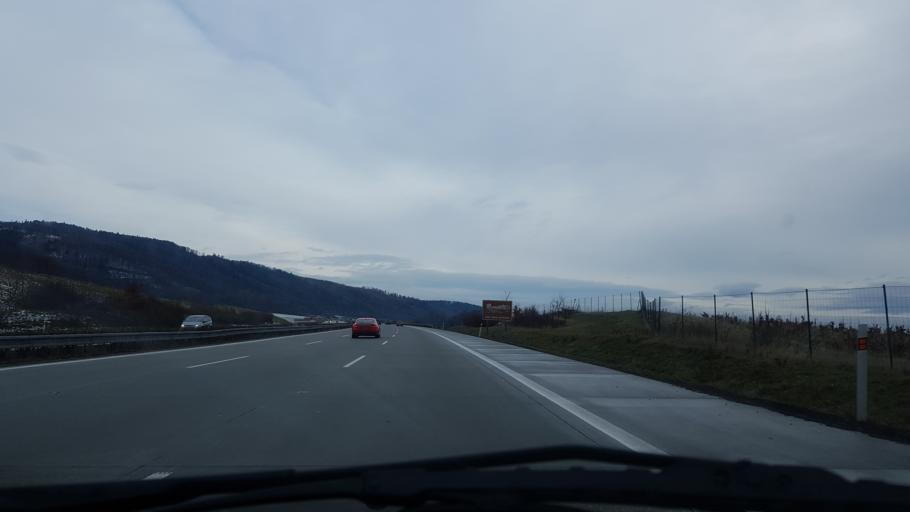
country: CZ
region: Olomoucky
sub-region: Okres Prerov
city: Lipnik nad Becvou
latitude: 49.5651
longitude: 17.6363
